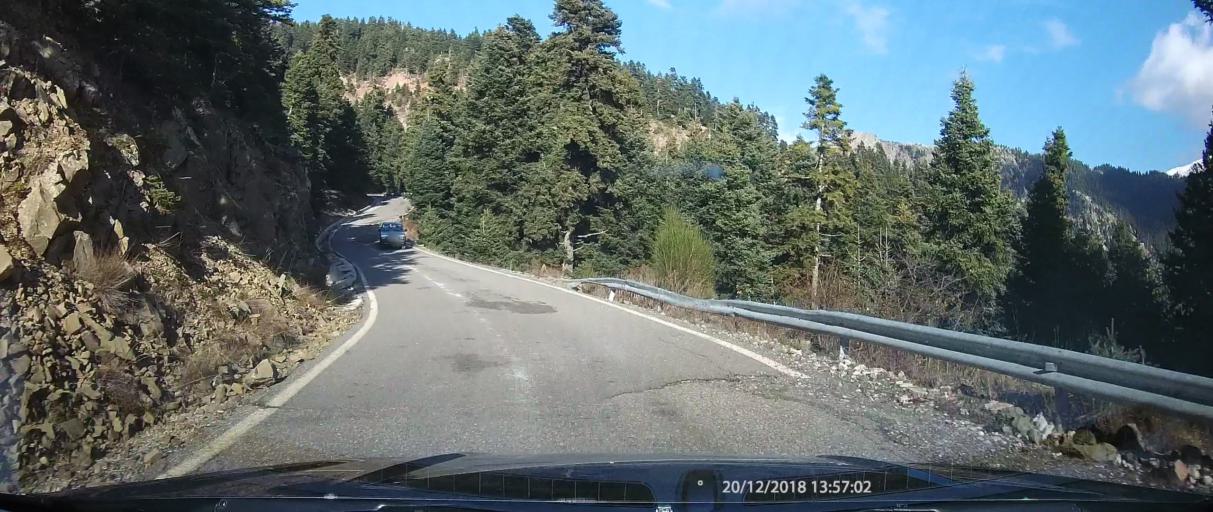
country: GR
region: West Greece
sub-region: Nomos Aitolias kai Akarnanias
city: Thermo
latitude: 38.7078
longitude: 21.6199
